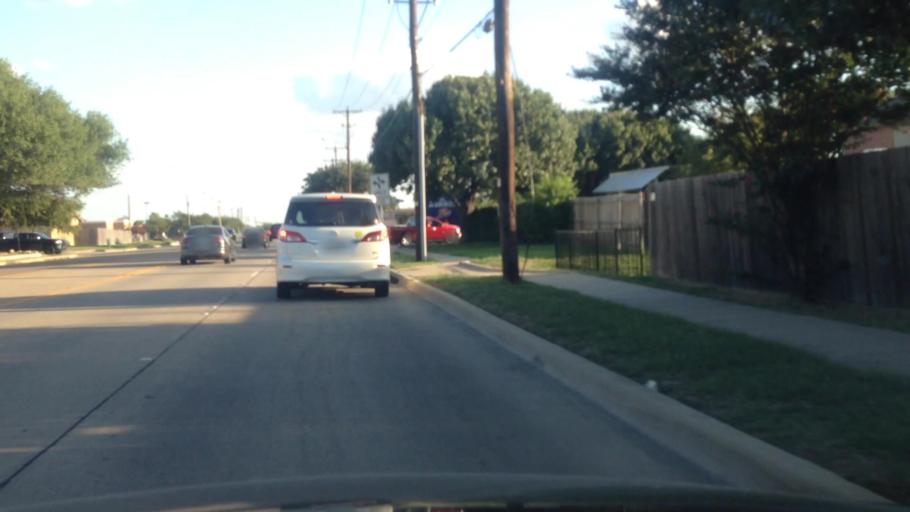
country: US
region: Texas
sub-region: Tarrant County
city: Watauga
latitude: 32.8788
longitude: -97.2380
